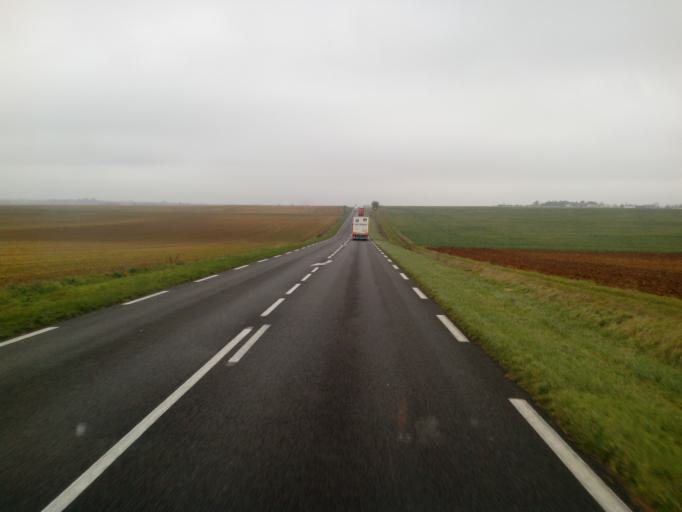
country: FR
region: Poitou-Charentes
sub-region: Departement de la Vienne
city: Cisse
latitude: 46.6339
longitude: 0.2312
